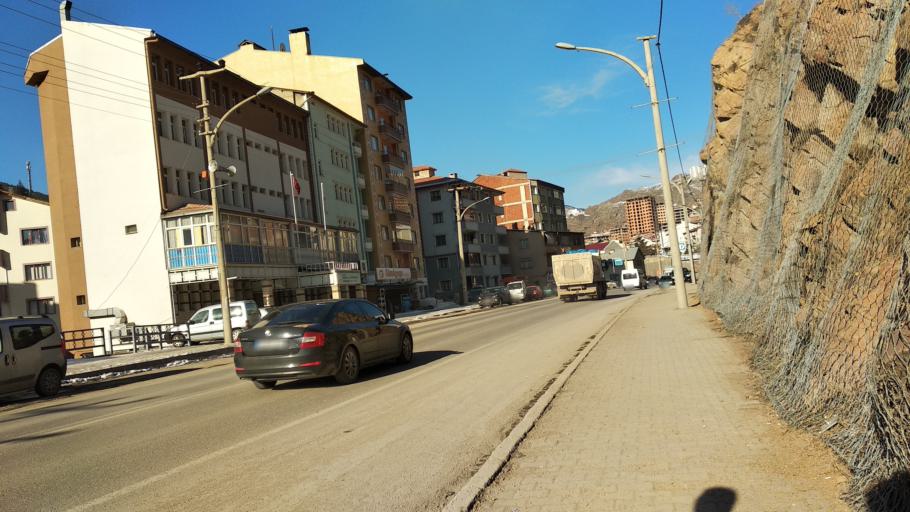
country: TR
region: Gumushane
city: Gumushkhane
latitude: 40.4556
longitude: 39.4909
